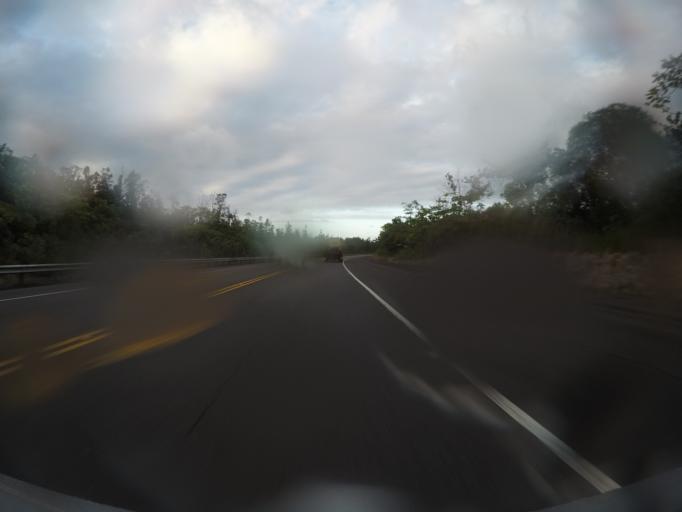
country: US
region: Hawaii
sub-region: Hawaii County
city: Hilo
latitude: 19.6906
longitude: -155.1152
